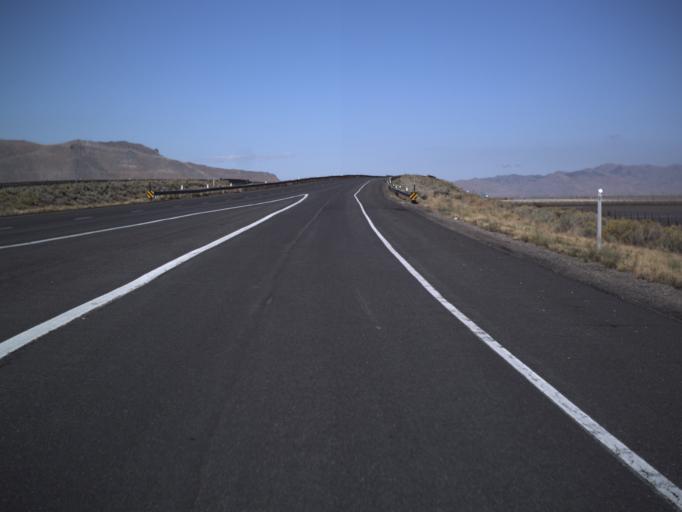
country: US
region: Utah
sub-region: Tooele County
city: Grantsville
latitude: 40.7080
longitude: -112.5245
